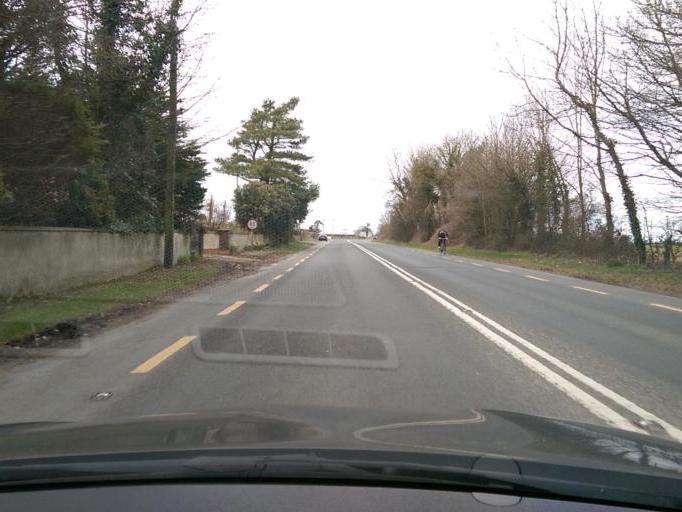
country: IE
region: Leinster
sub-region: An Iarmhi
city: Athlone
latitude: 53.3866
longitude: -7.9919
